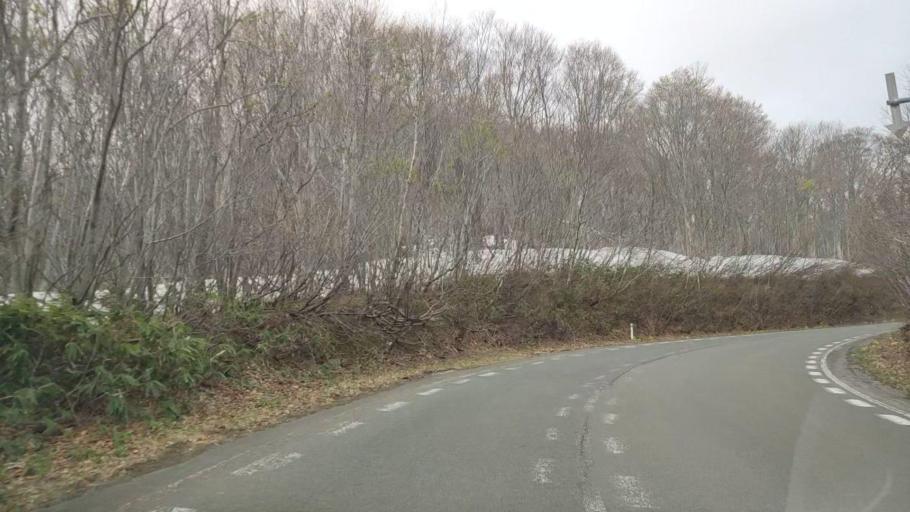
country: JP
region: Aomori
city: Aomori Shi
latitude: 40.6572
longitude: 140.9586
